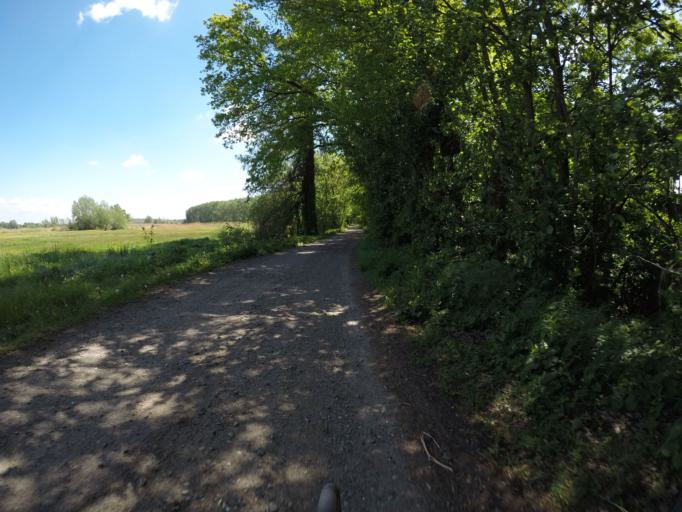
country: DE
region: Brandenburg
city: Werder
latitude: 52.4247
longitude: 12.9399
